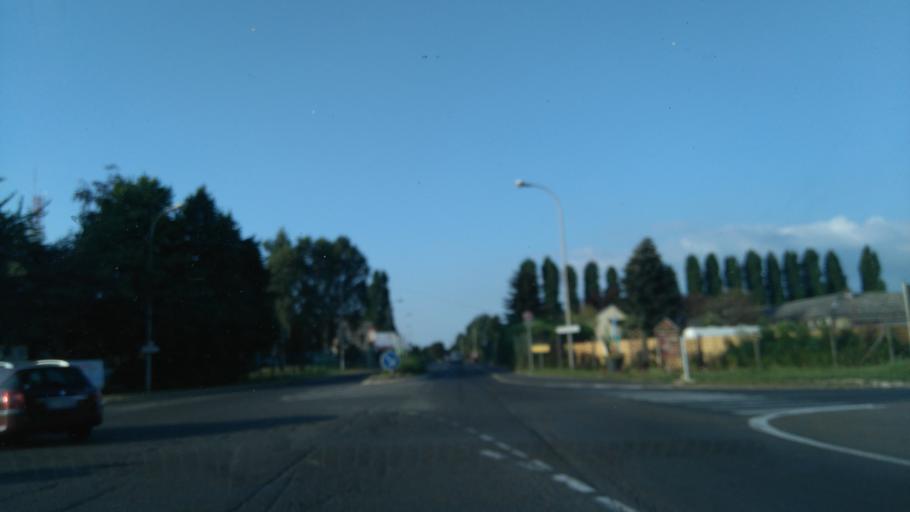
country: FR
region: Picardie
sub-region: Departement de l'Oise
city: Creil
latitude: 49.2460
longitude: 2.4705
